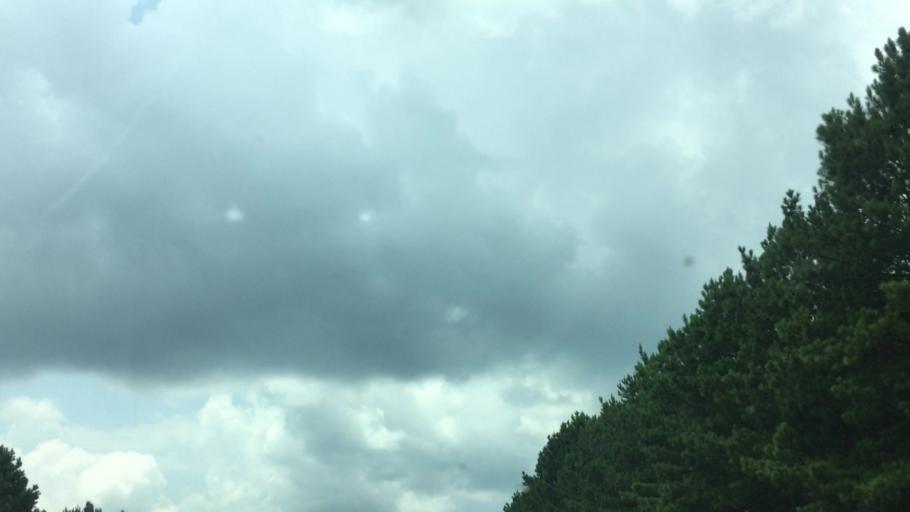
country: US
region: Georgia
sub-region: Fulton County
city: Fairburn
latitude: 33.6076
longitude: -84.6206
